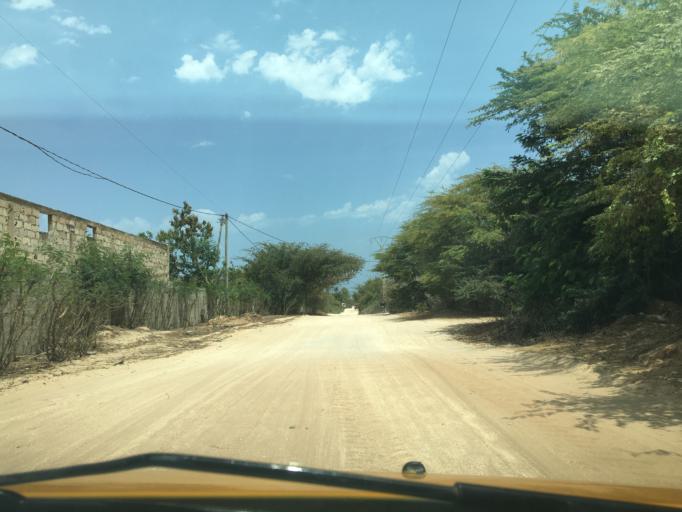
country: SN
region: Thies
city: Thies
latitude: 14.8214
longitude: -17.2021
